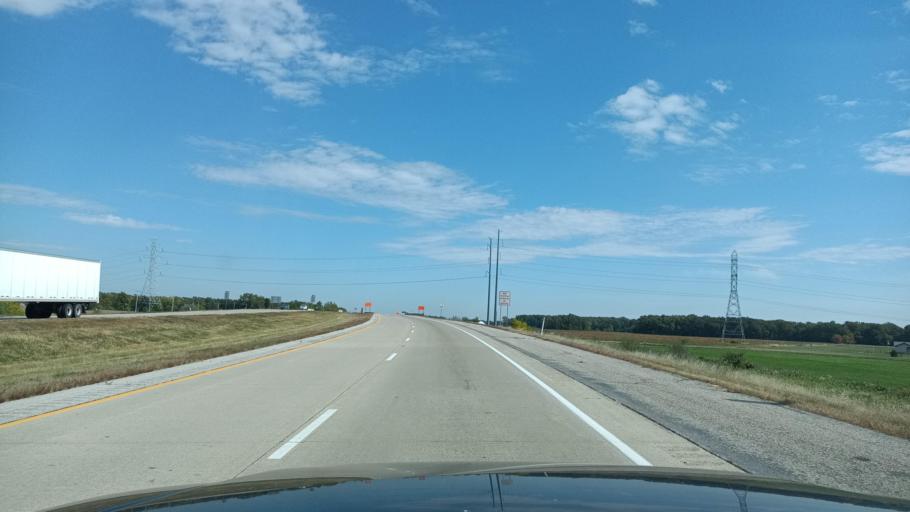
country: US
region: Indiana
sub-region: Allen County
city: New Haven
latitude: 41.0885
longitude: -84.9849
